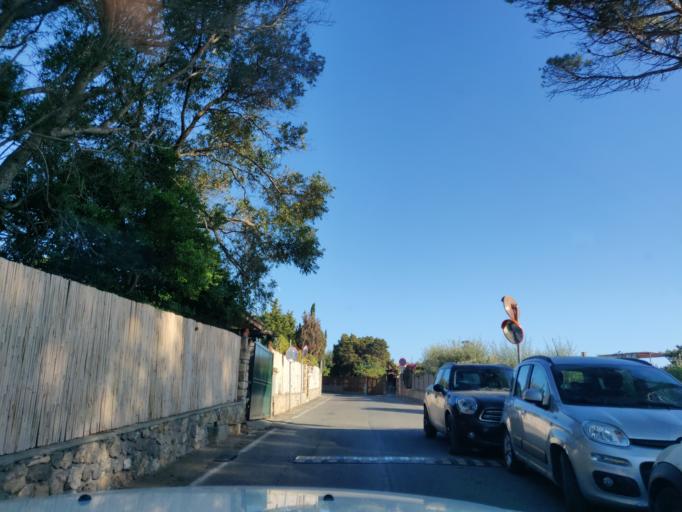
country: IT
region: Tuscany
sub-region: Provincia di Grosseto
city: Orbetello Scalo
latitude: 42.4082
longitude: 11.2836
